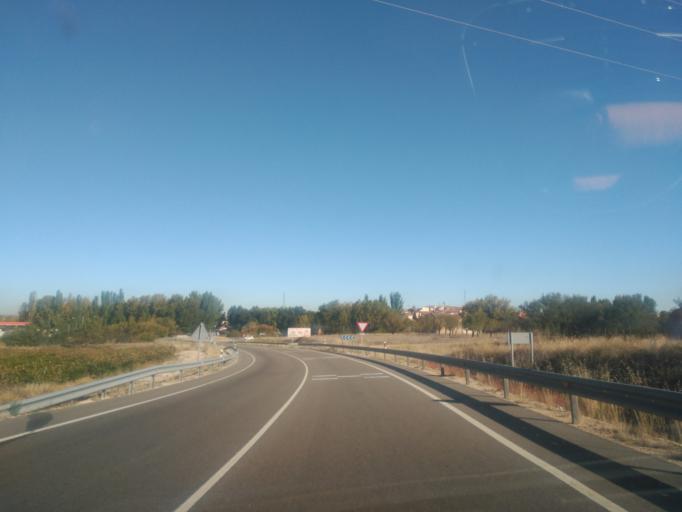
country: ES
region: Castille and Leon
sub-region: Provincia de Burgos
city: Castrillo de la Vega
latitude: 41.6465
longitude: -3.7812
